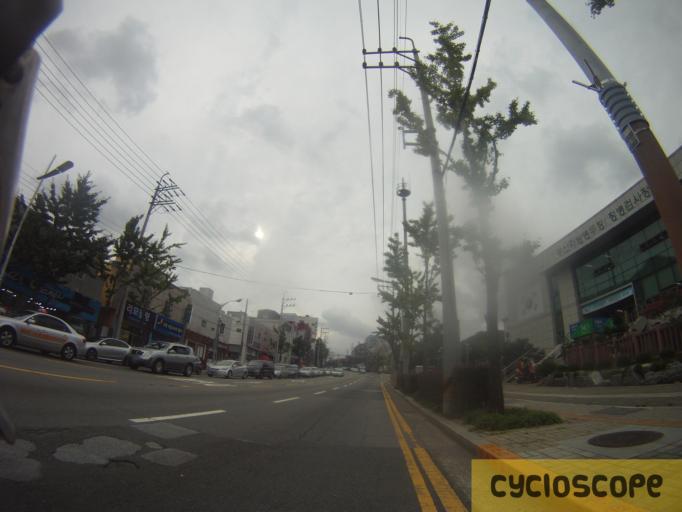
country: KR
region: Busan
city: Busan
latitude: 35.1732
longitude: 129.1014
